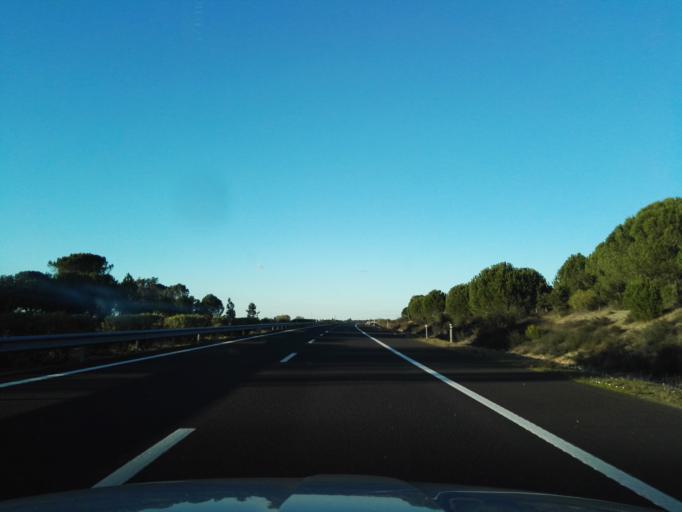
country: PT
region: Santarem
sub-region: Benavente
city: Poceirao
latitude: 38.7499
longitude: -8.6835
